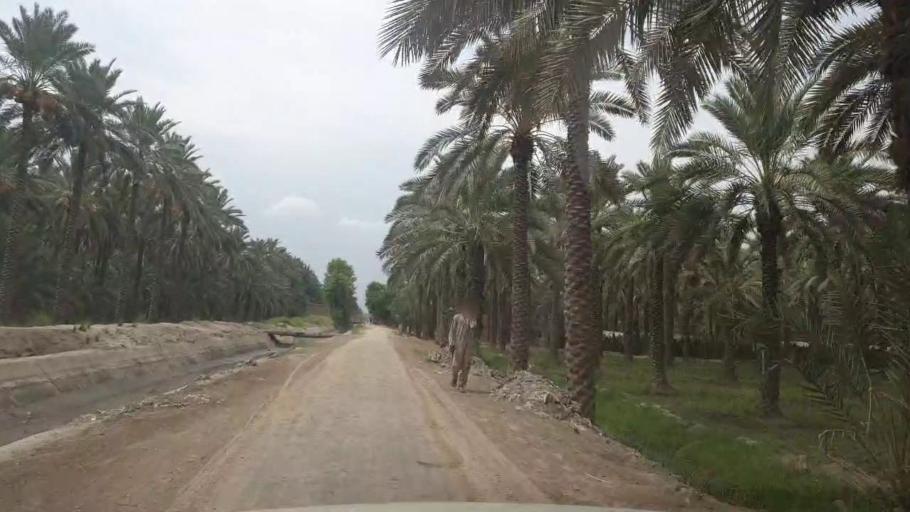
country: PK
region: Sindh
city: Sukkur
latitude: 27.6202
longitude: 68.8064
